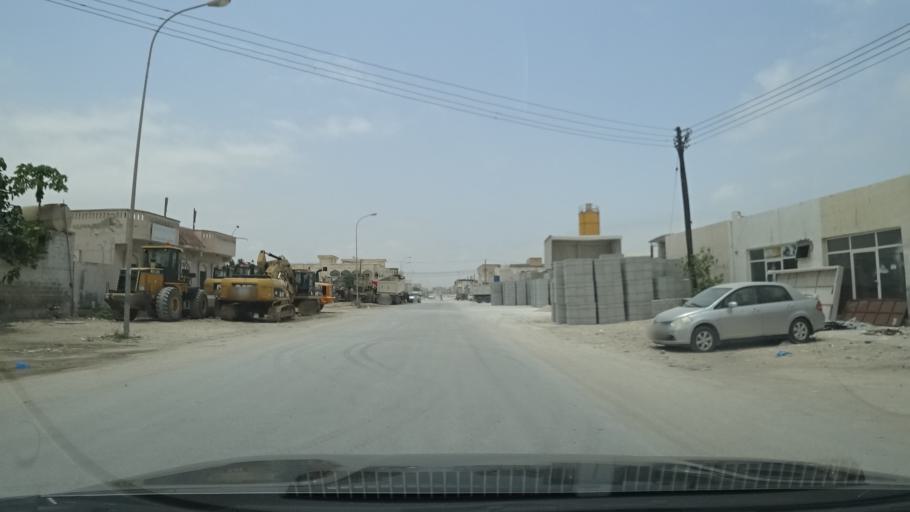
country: OM
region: Zufar
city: Salalah
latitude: 17.0173
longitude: 54.0476
